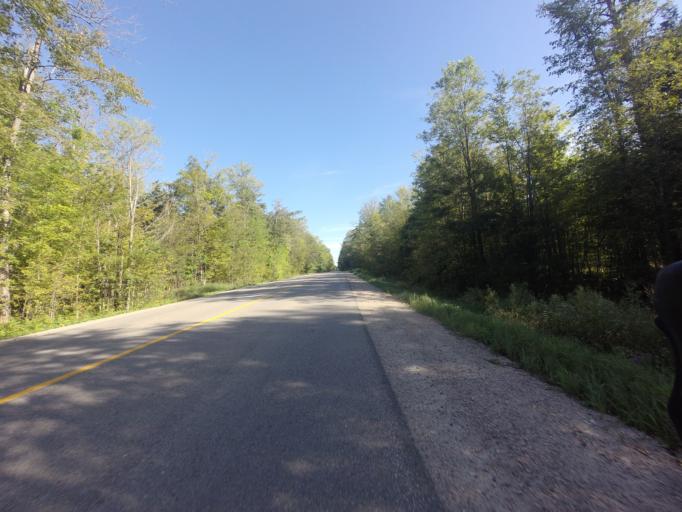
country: CA
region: Ontario
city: Perth
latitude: 44.8984
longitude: -76.3281
